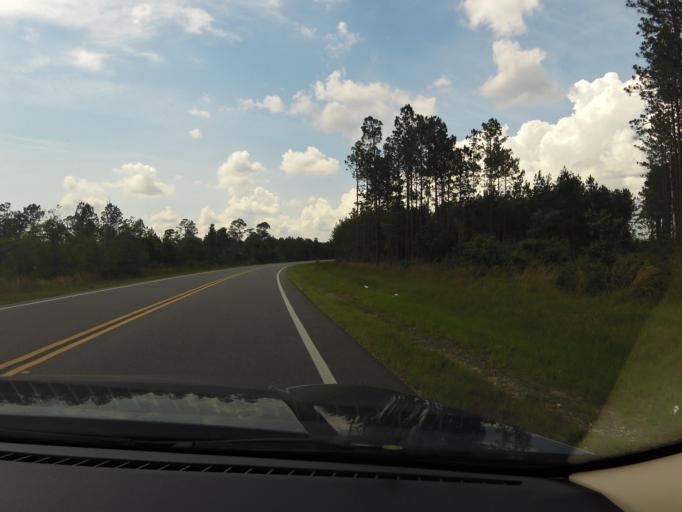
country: US
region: Florida
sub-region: Baker County
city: Macclenny
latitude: 30.2187
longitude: -82.0738
